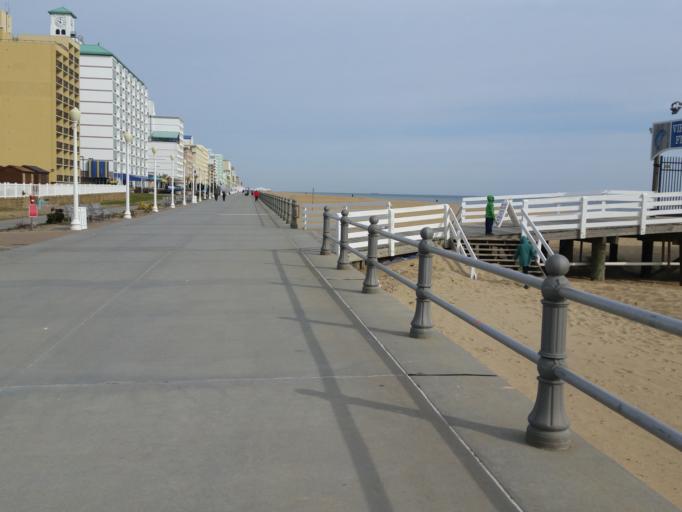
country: US
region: Virginia
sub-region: City of Virginia Beach
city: Virginia Beach
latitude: 36.8431
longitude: -75.9727
